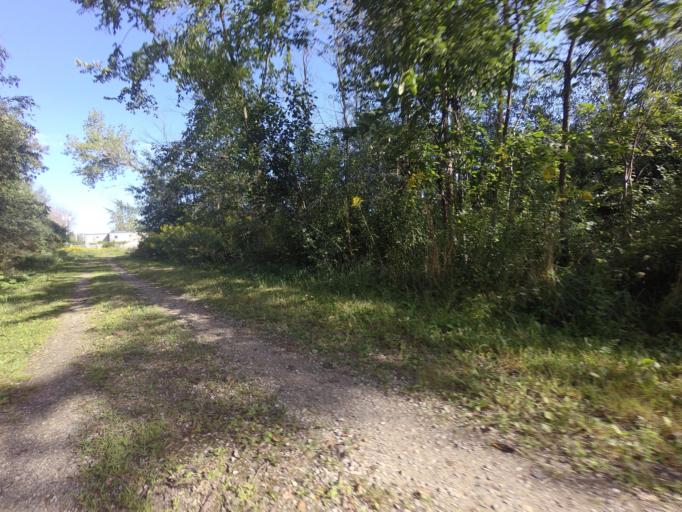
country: CA
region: Ontario
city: Waterloo
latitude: 43.6652
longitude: -80.4357
